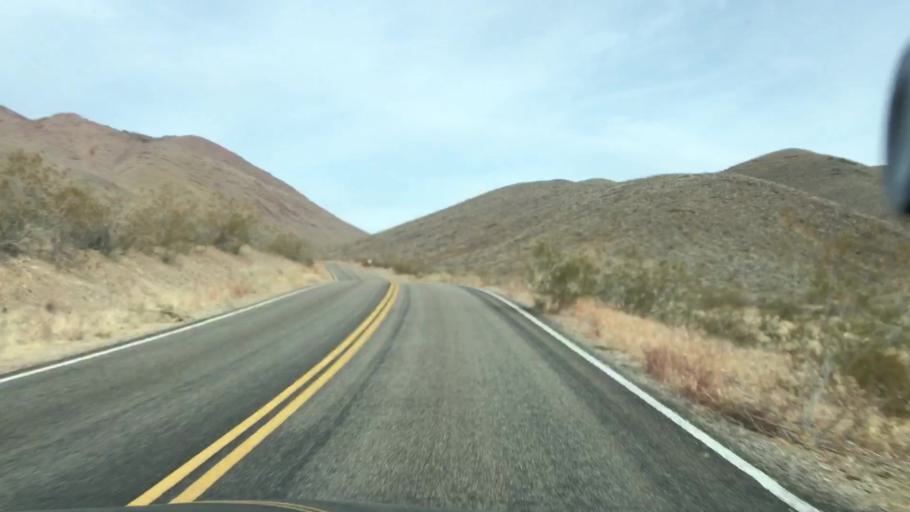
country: US
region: Nevada
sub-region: Nye County
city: Beatty
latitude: 36.7678
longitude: -116.9298
